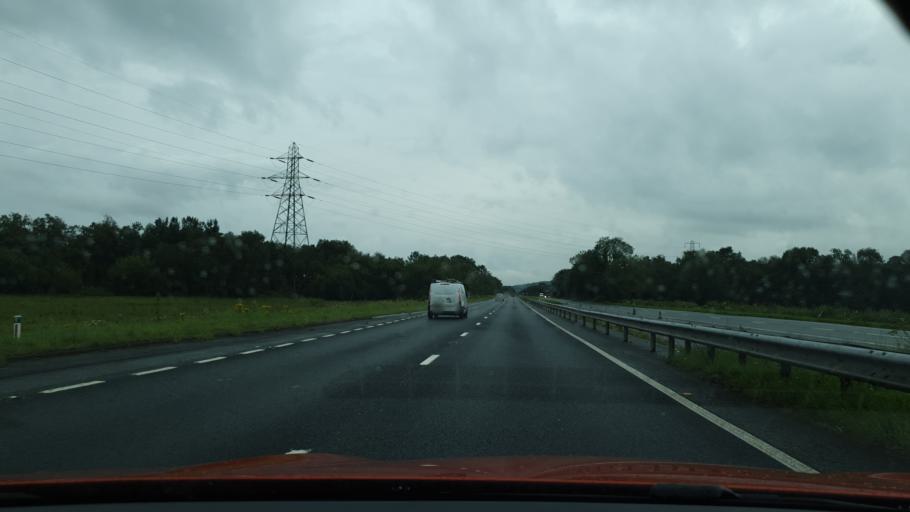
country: GB
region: England
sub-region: Cumbria
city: Arnside
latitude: 54.2334
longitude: -2.8618
